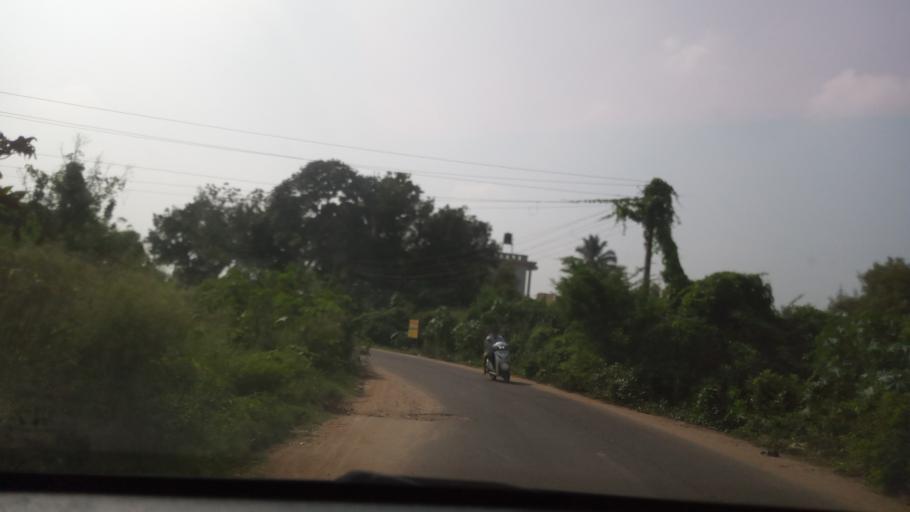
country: IN
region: Tamil Nadu
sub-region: Coimbatore
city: Perur
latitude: 11.0068
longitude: 76.8881
